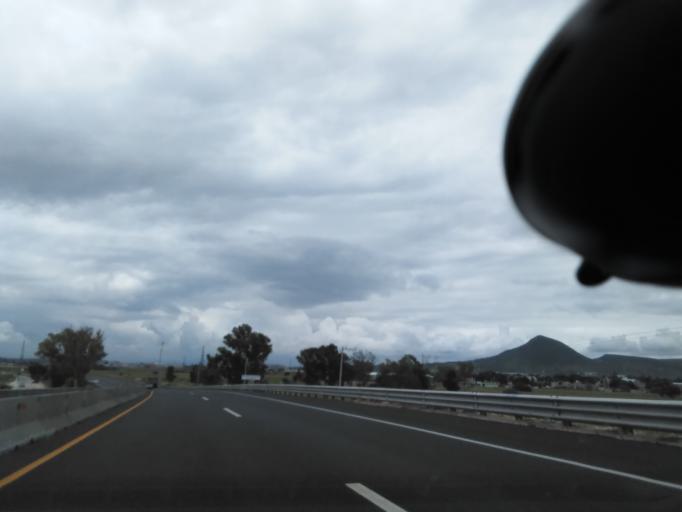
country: MX
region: Mexico
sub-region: Huehuetoca
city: Casa Nueva
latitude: 19.8237
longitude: -99.2178
